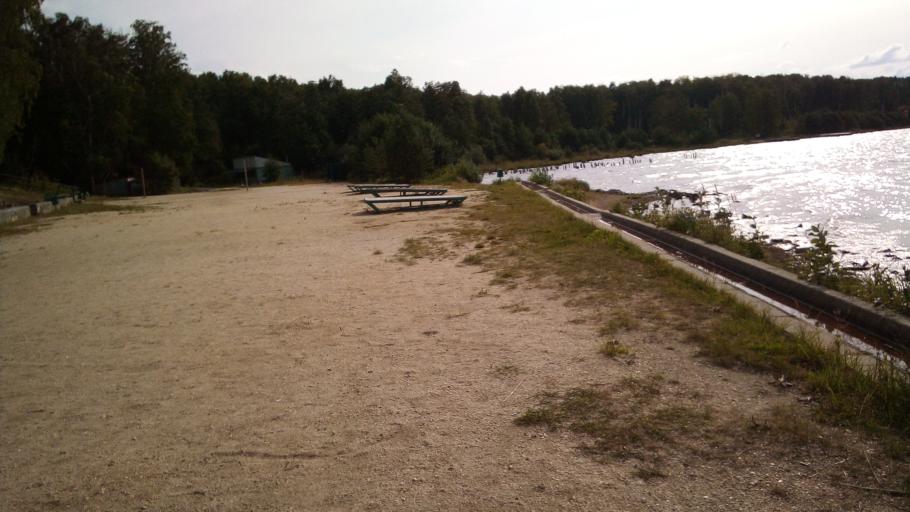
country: RU
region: Chelyabinsk
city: Tayginka
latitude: 55.4763
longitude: 60.4892
